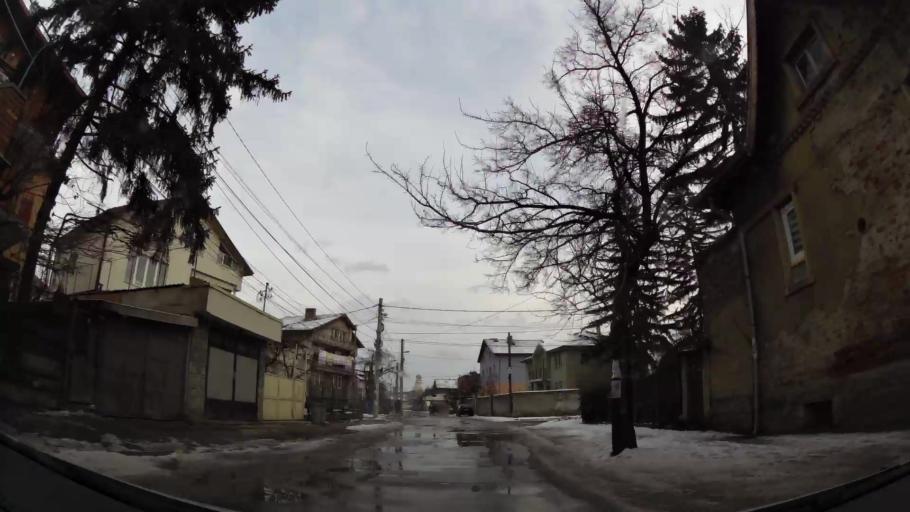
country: BG
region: Sofia-Capital
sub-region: Stolichna Obshtina
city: Sofia
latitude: 42.7183
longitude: 23.3453
